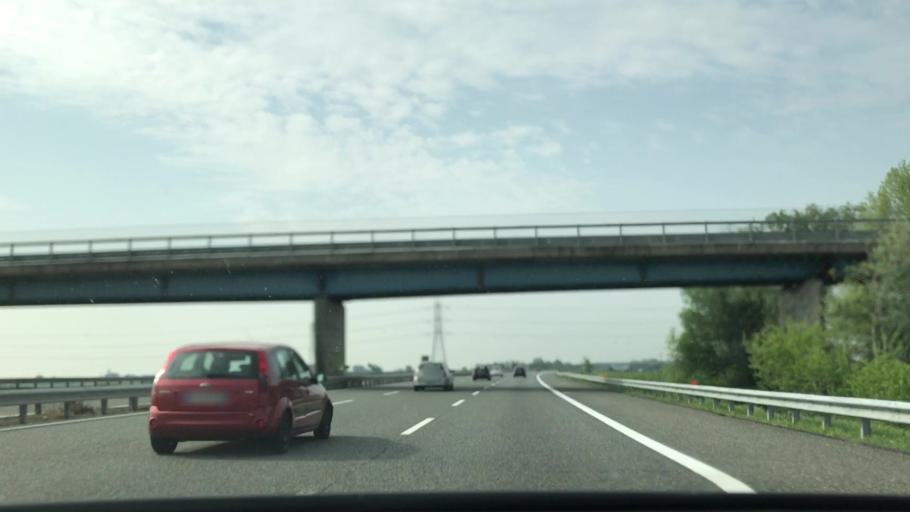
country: IT
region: Piedmont
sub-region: Provincia di Vercelli
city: Prarolo
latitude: 45.2802
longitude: 8.4714
